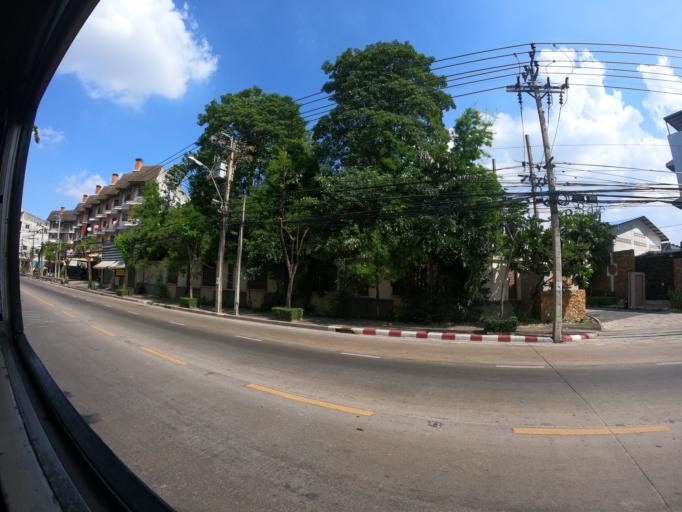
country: TH
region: Bangkok
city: Lat Phrao
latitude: 13.8124
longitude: 100.6104
